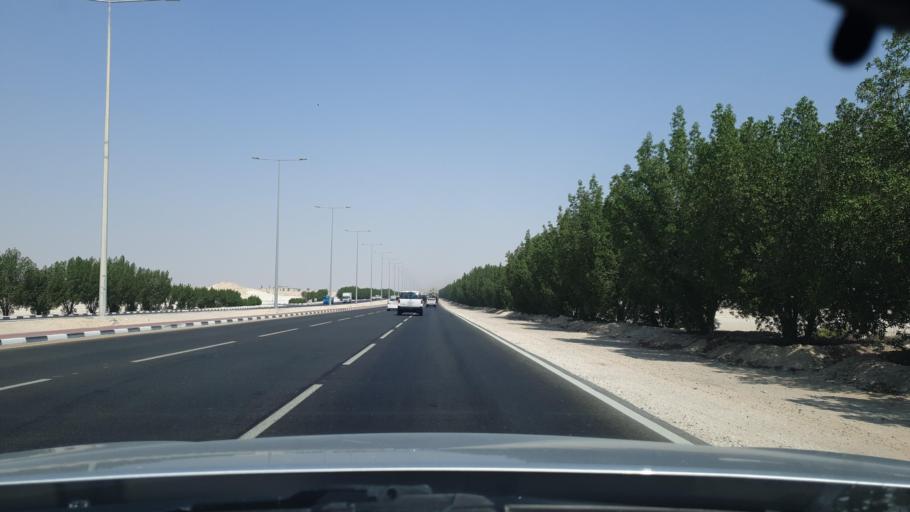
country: QA
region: Al Khawr
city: Al Khawr
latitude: 25.6969
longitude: 51.5022
